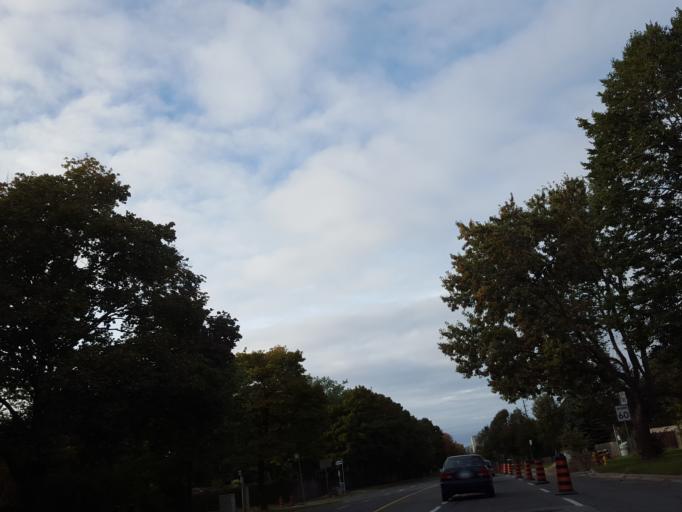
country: CA
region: Ontario
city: Scarborough
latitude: 43.7804
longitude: -79.3087
